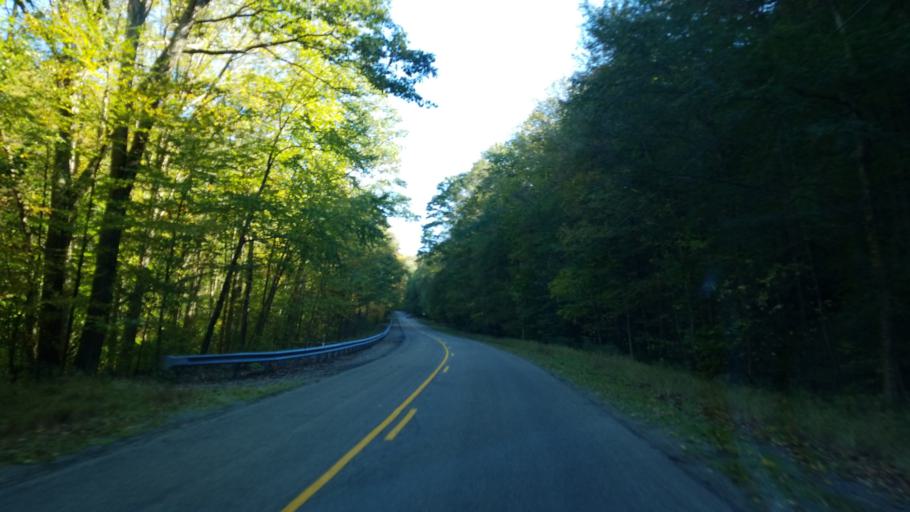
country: US
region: Pennsylvania
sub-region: Clearfield County
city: Shiloh
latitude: 41.2550
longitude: -78.3852
